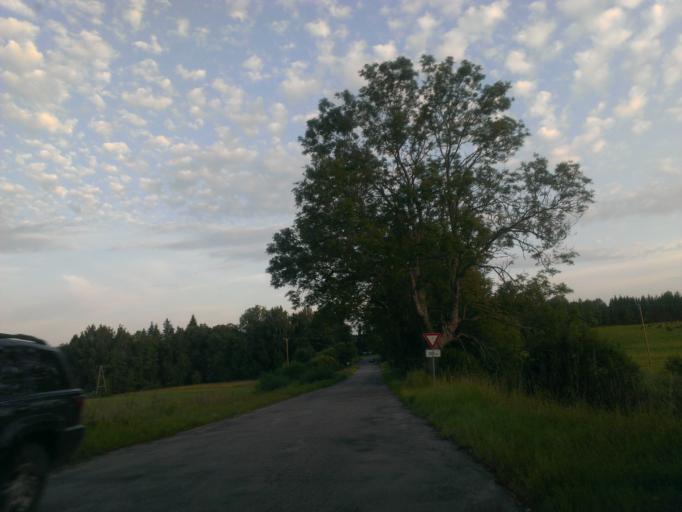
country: LV
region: Amatas Novads
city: Drabesi
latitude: 57.2413
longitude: 25.2829
